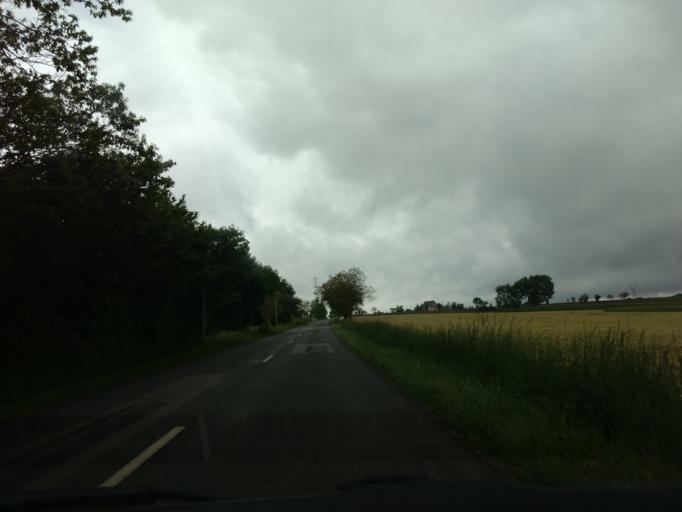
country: FR
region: Midi-Pyrenees
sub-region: Departement de l'Aveyron
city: Montbazens
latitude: 44.5006
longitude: 2.1992
